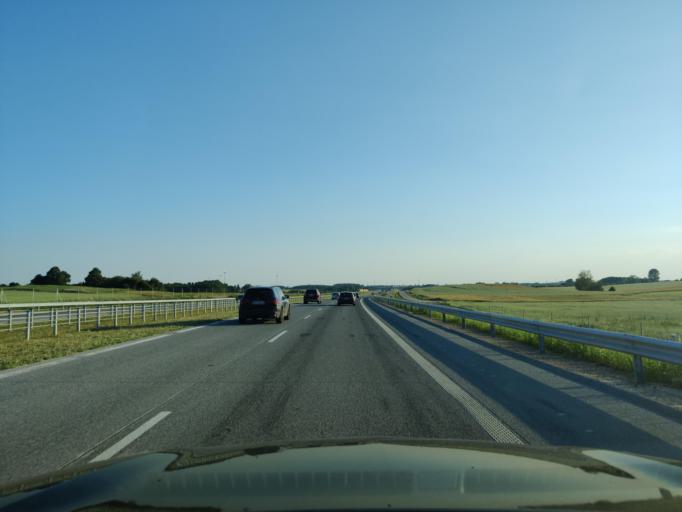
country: PL
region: Masovian Voivodeship
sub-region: Powiat mlawski
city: Mlawa
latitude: 53.0870
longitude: 20.4031
